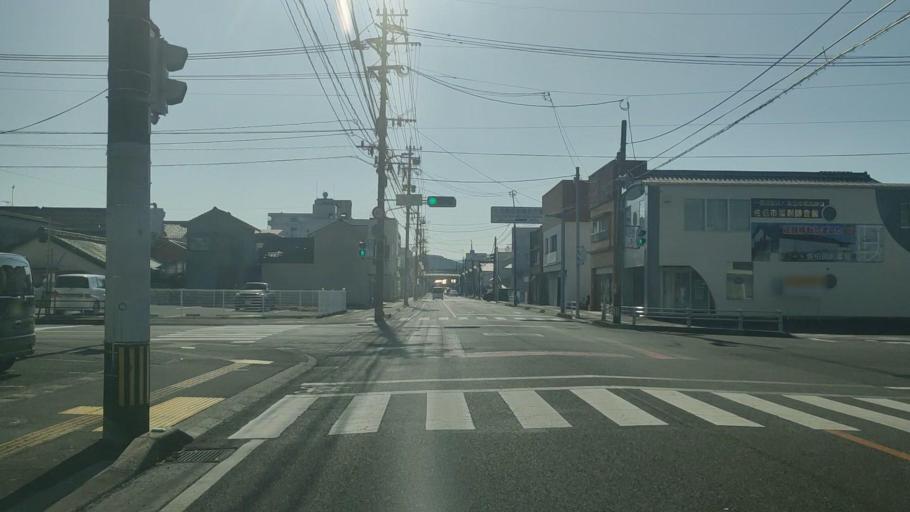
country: JP
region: Oita
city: Saiki
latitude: 32.9656
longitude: 131.9013
